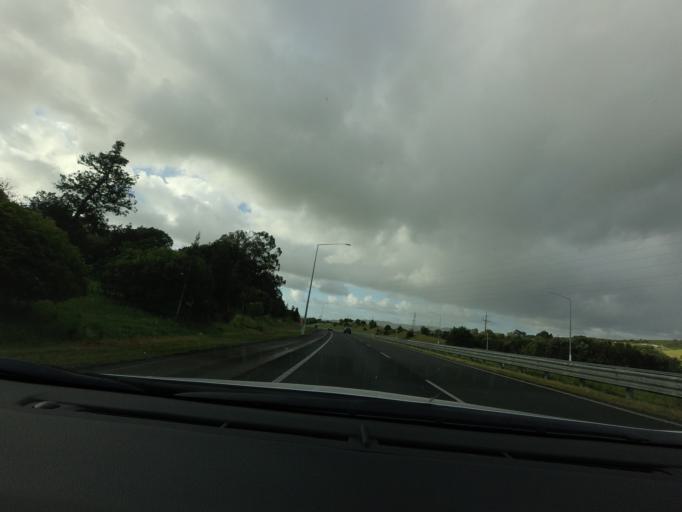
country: NZ
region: Auckland
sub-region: Auckland
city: Pukekohe East
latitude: -37.1698
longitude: 174.9846
